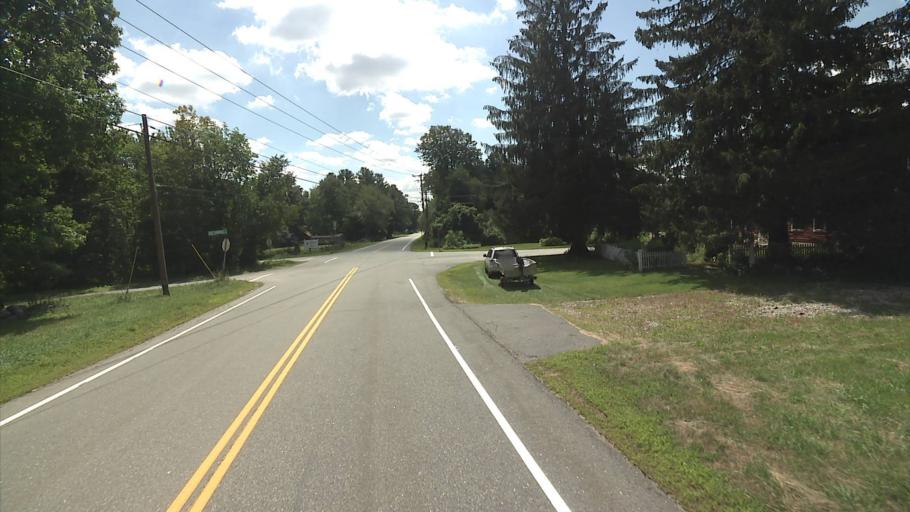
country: US
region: Massachusetts
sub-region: Worcester County
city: Southbridge
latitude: 41.9689
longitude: -72.0815
